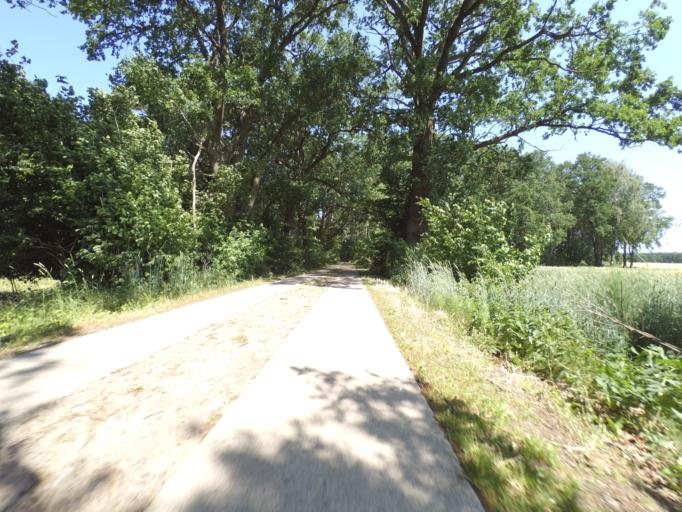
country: DE
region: Brandenburg
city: Heiligengrabe
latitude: 53.2379
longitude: 12.3149
